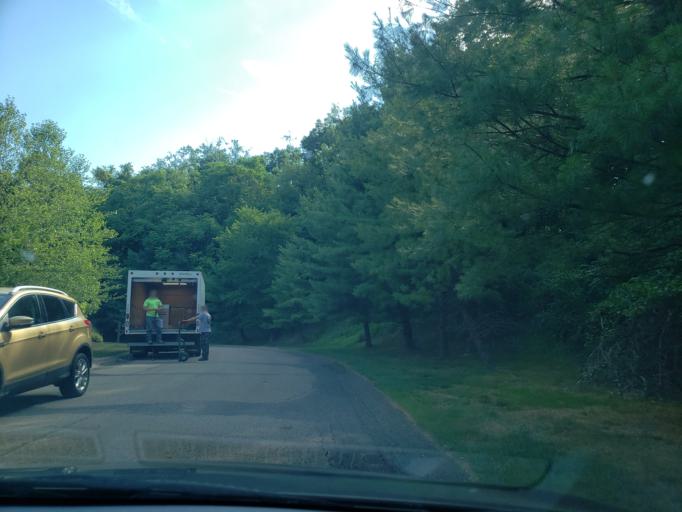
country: US
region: Pennsylvania
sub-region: Allegheny County
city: Coraopolis
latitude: 40.5399
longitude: -80.1471
